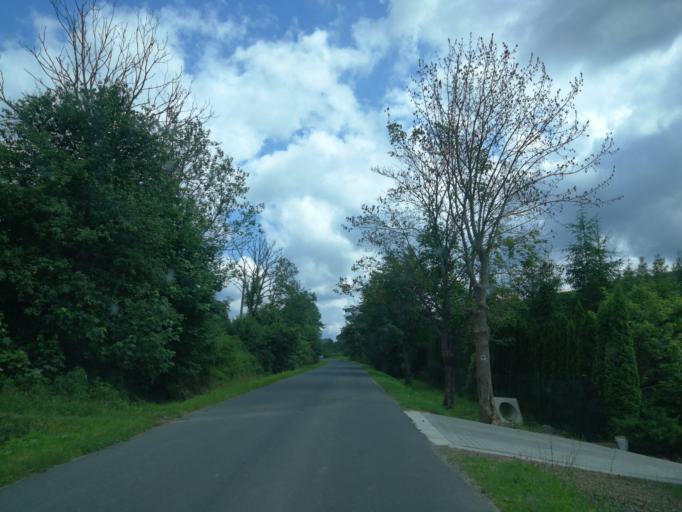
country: PL
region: Subcarpathian Voivodeship
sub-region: Powiat leski
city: Polanczyk
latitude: 49.4200
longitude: 22.4281
